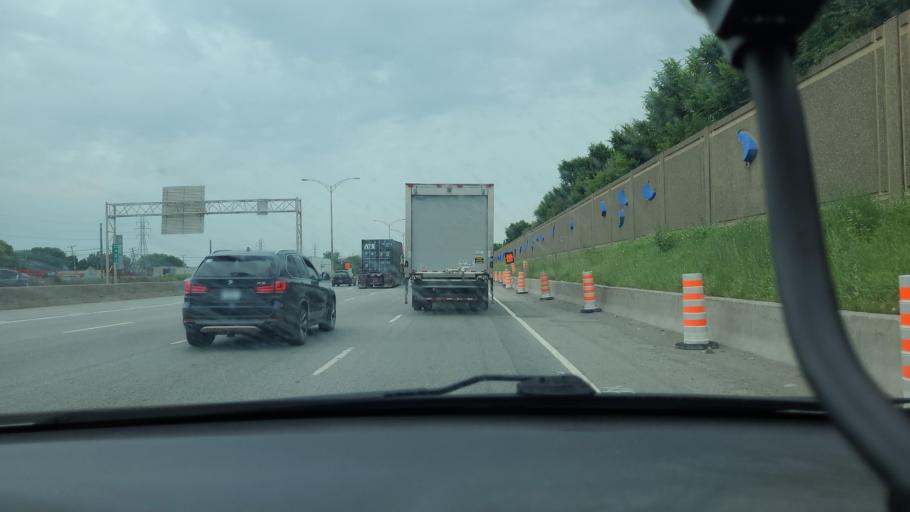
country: CA
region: Quebec
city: Cote-Saint-Luc
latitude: 45.4473
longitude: -73.6836
